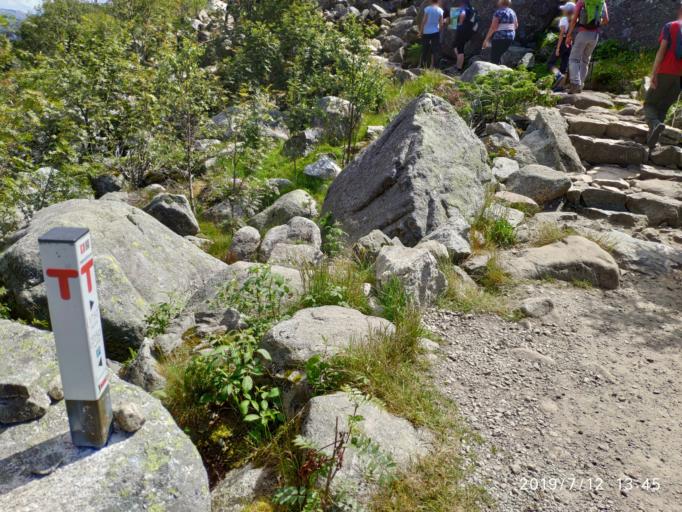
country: NO
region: Rogaland
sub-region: Forsand
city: Forsand
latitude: 58.9912
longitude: 6.1685
